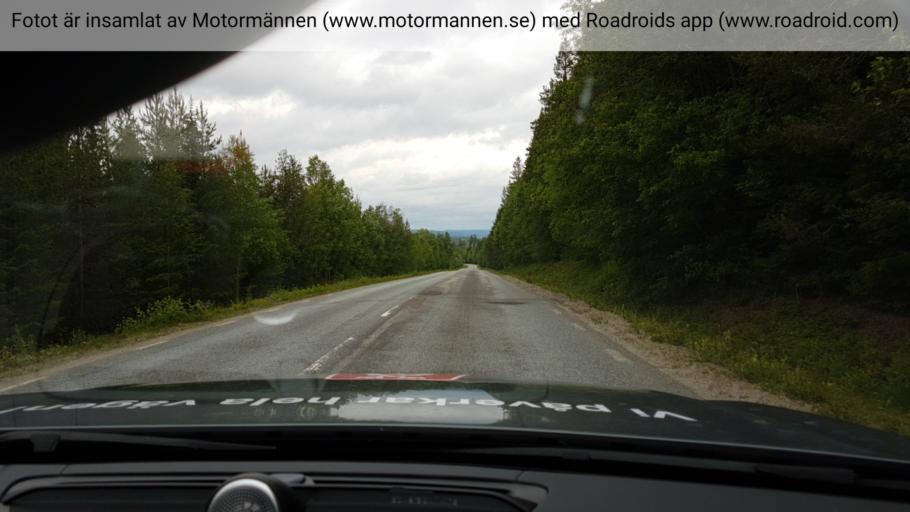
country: SE
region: Jaemtland
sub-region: Braecke Kommun
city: Braecke
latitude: 62.8095
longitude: 15.4641
